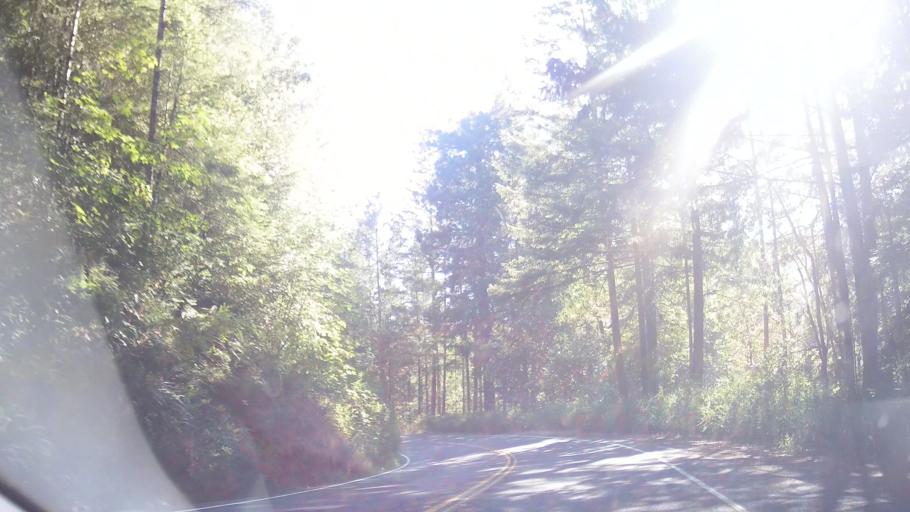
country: US
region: California
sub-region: Mendocino County
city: Brooktrails
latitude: 39.3702
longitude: -123.4964
